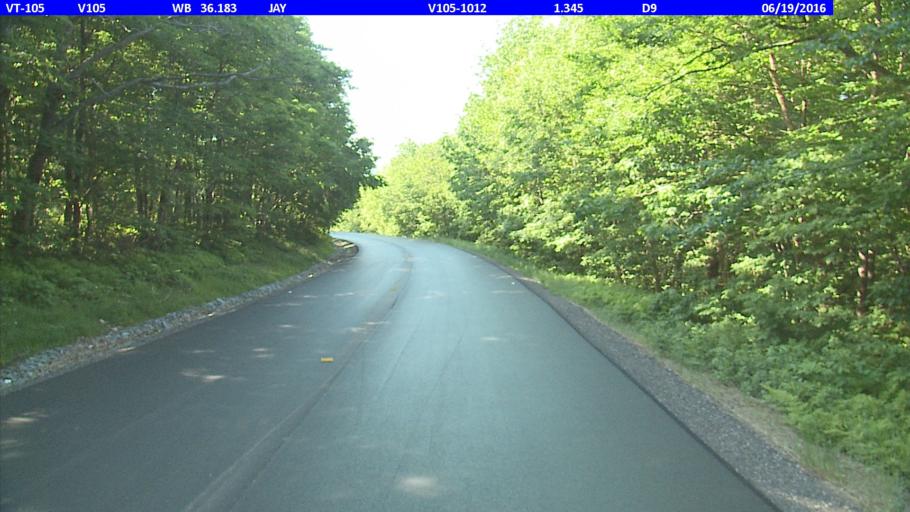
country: US
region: Vermont
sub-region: Franklin County
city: Richford
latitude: 44.9769
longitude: -72.5278
